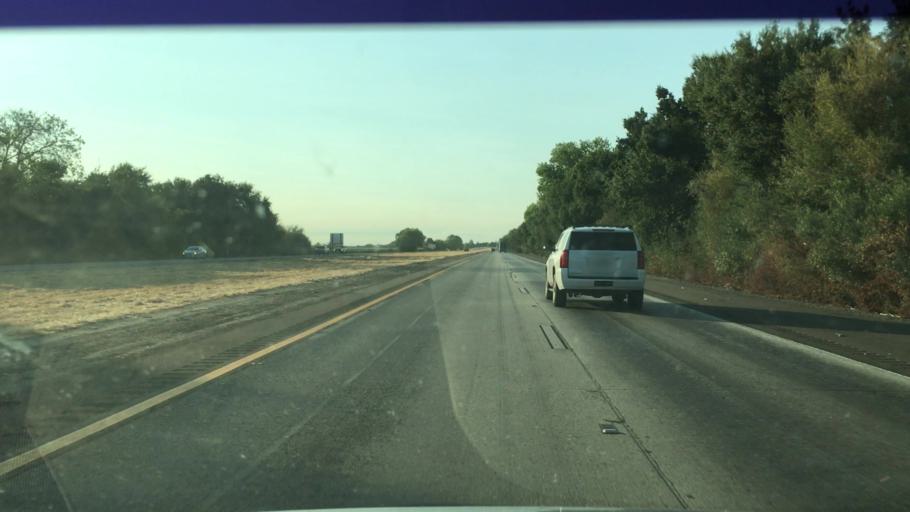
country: US
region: California
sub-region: San Joaquin County
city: Thornton
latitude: 38.2309
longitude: -121.4340
